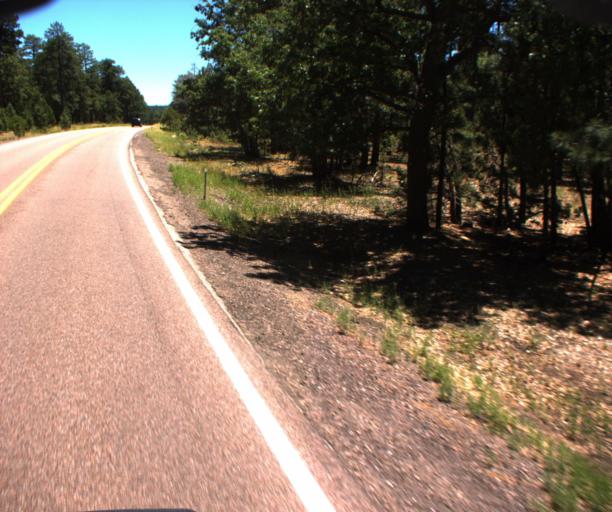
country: US
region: Arizona
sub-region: Gila County
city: Pine
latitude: 34.4416
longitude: -111.4883
